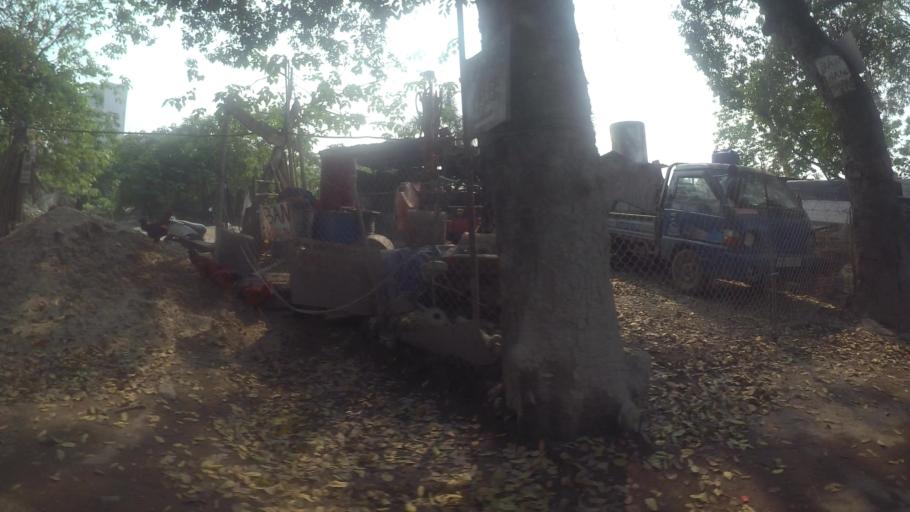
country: VN
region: Ha Noi
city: Ha Dong
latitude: 20.9965
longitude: 105.7525
